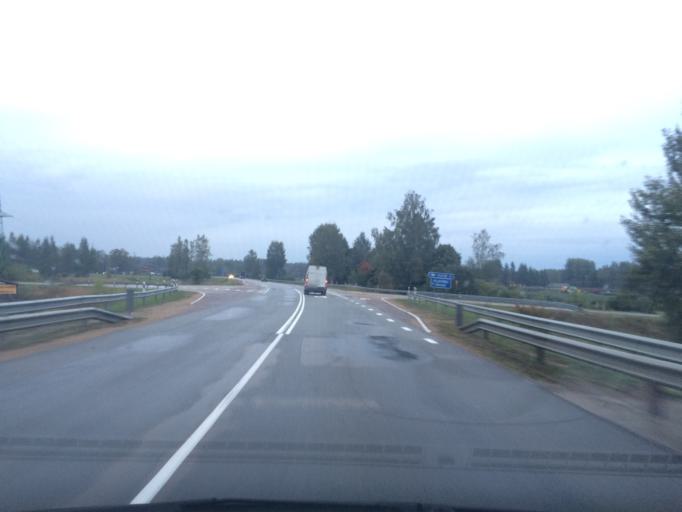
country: LV
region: Plavinu
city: Plavinas
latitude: 56.6082
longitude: 25.7836
